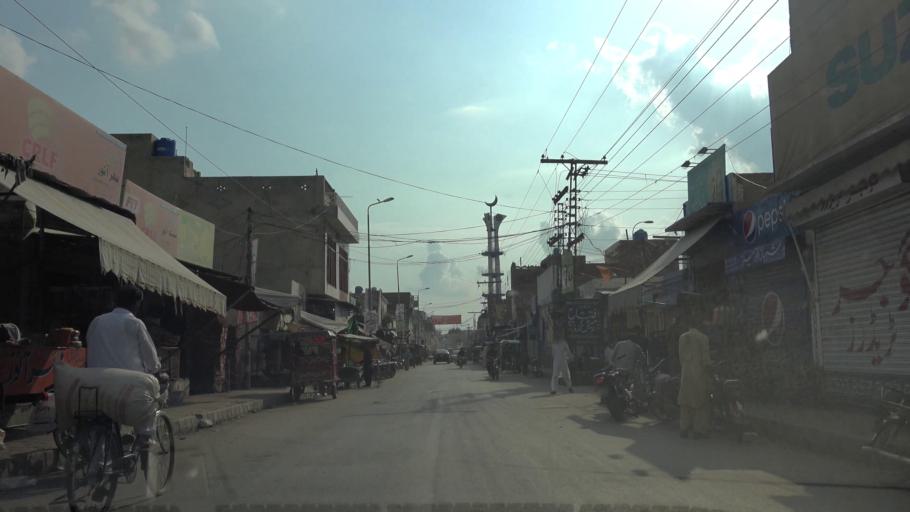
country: PK
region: Punjab
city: Nankana Sahib
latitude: 31.4483
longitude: 73.6998
